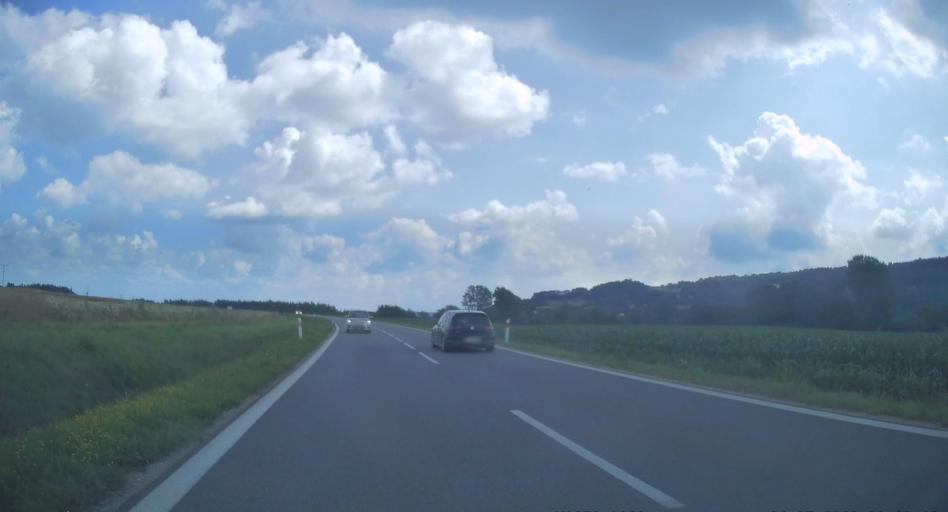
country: PL
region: Lesser Poland Voivodeship
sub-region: Powiat tarnowski
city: Wielka Wies
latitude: 49.9300
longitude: 20.8416
